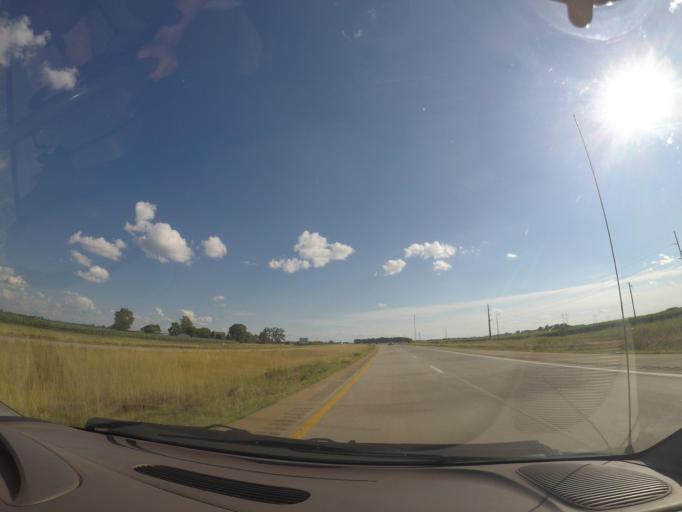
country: US
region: Ohio
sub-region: Lucas County
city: Whitehouse
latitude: 41.4943
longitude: -83.7663
